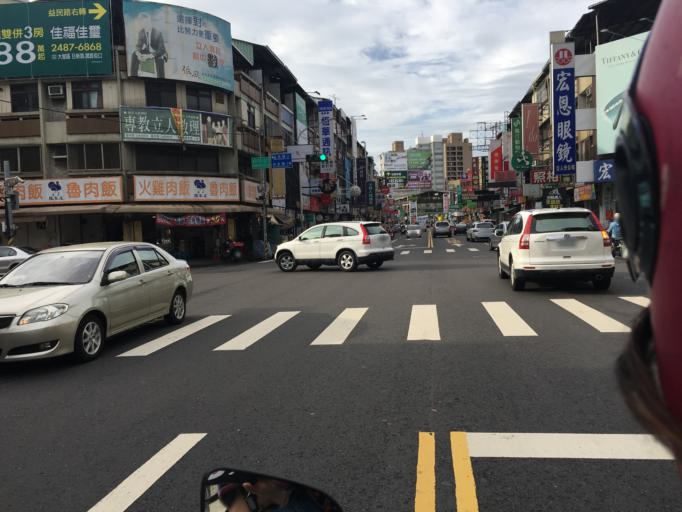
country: TW
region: Taiwan
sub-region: Taichung City
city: Taichung
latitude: 24.1061
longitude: 120.6895
